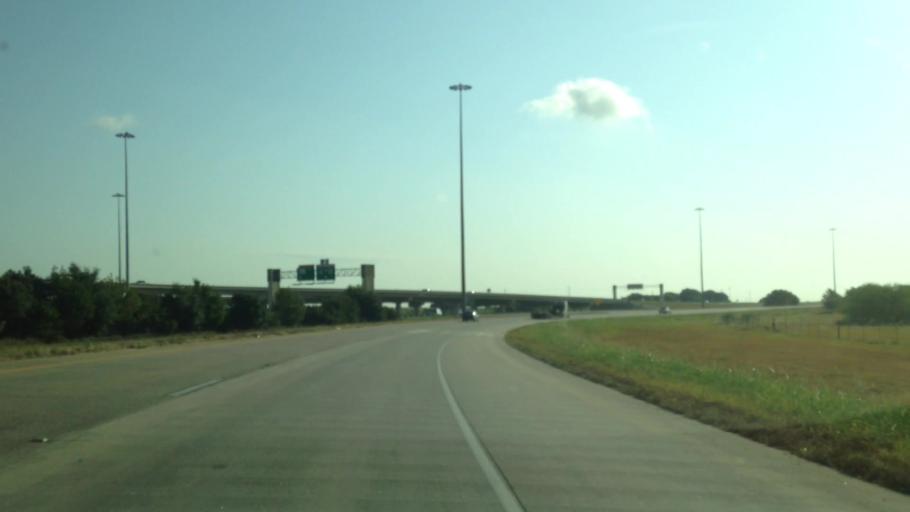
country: US
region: Texas
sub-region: Travis County
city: Onion Creek
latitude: 30.1102
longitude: -97.8068
